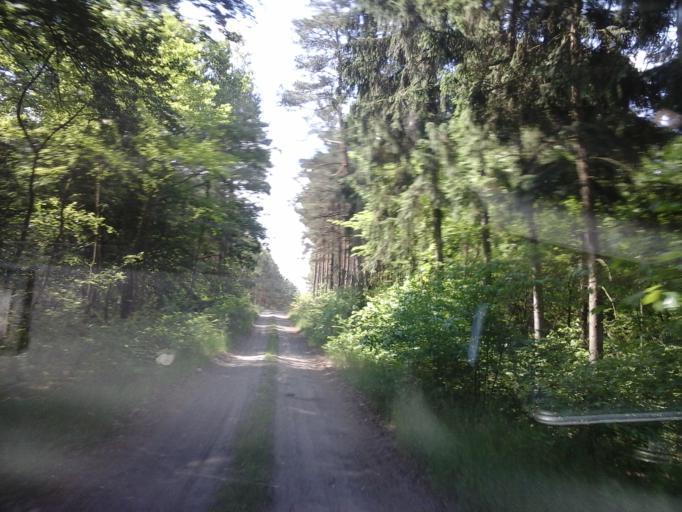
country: PL
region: West Pomeranian Voivodeship
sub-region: Powiat choszczenski
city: Bierzwnik
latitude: 53.1009
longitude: 15.6778
